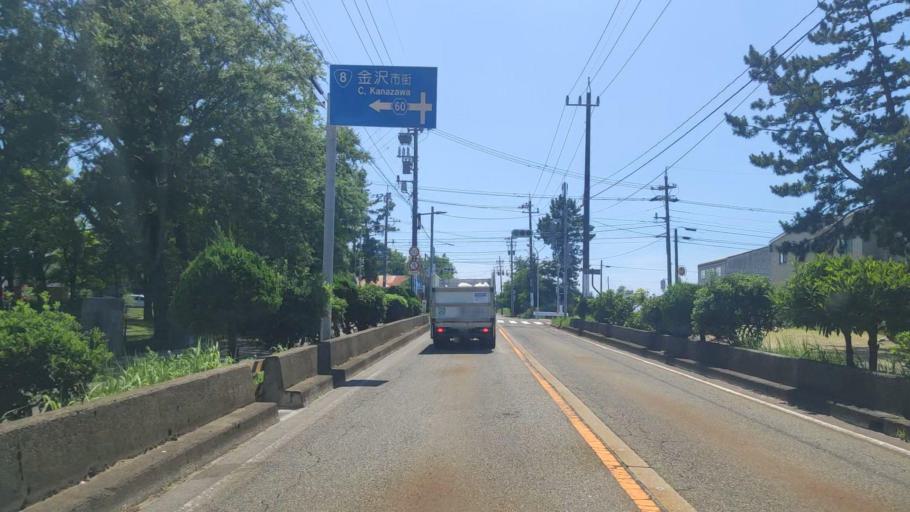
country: JP
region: Ishikawa
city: Kanazawa-shi
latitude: 36.6273
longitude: 136.6207
